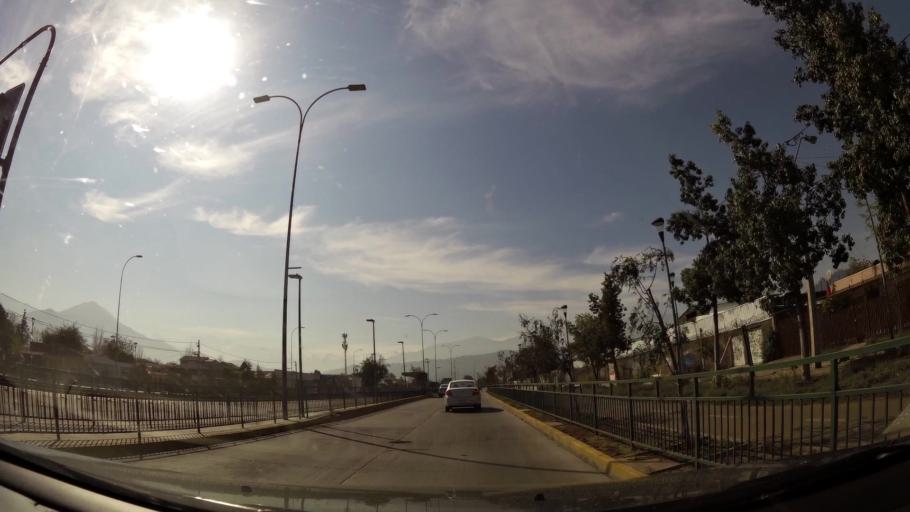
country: CL
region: Santiago Metropolitan
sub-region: Provincia de Santiago
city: Santiago
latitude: -33.3961
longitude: -70.6476
